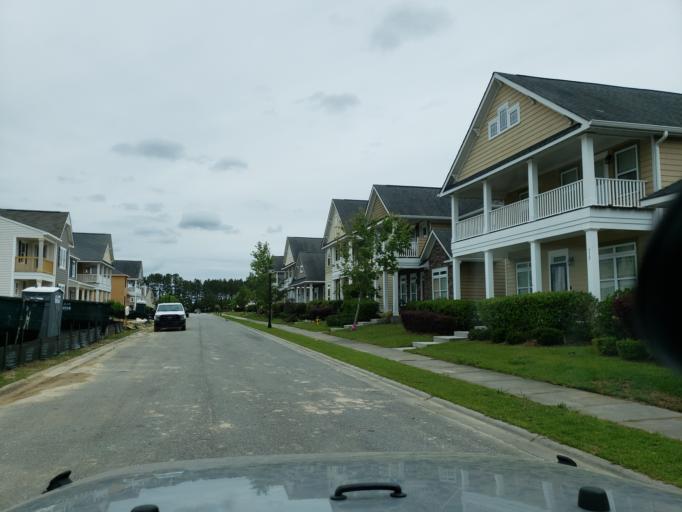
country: US
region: Georgia
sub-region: Chatham County
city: Port Wentworth
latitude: 32.2129
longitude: -81.1827
